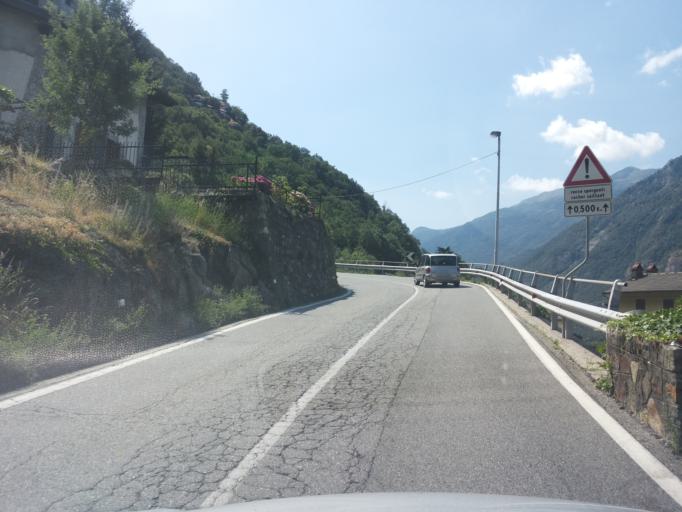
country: IT
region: Aosta Valley
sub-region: Valle d'Aosta
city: Pont-Saint-Martin
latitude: 45.5953
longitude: 7.8029
